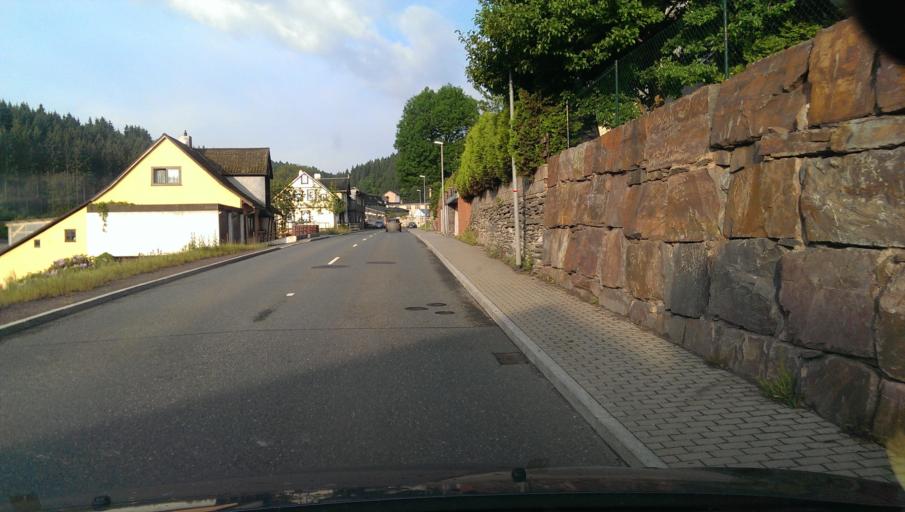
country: DE
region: Thuringia
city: Lichte
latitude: 50.5196
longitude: 11.1823
